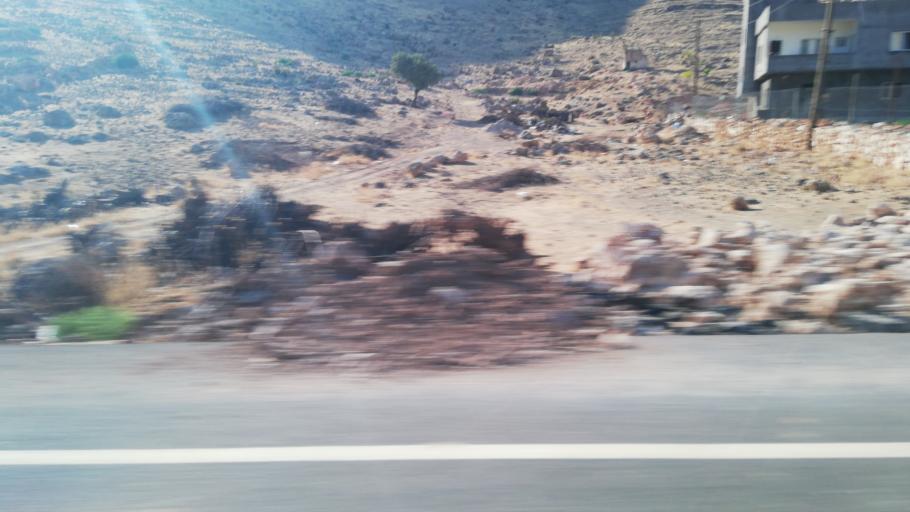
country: TR
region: Mardin
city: Sivrice
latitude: 37.2292
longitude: 41.3293
